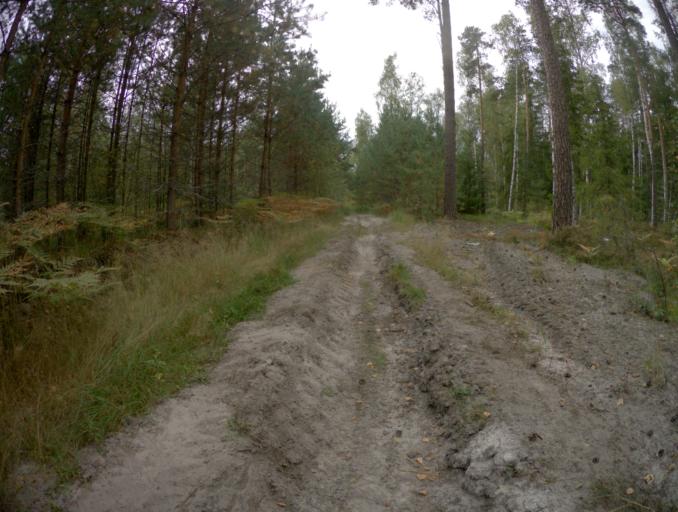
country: RU
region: Vladimir
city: Urshel'skiy
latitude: 55.8191
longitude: 40.2698
